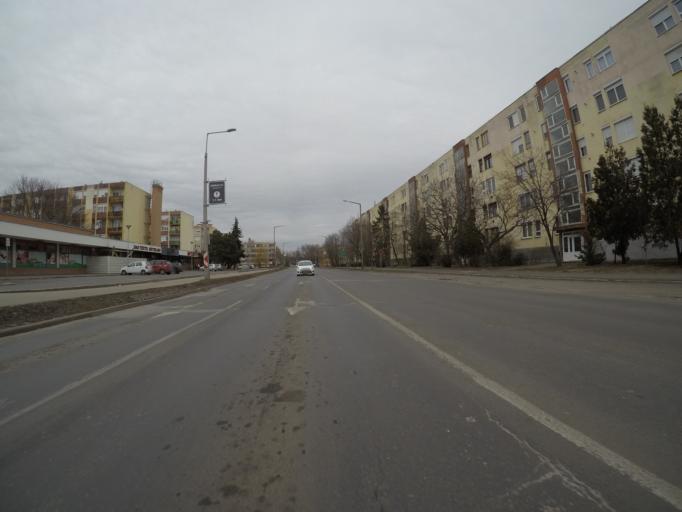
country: HU
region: Jasz-Nagykun-Szolnok
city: Jaszbereny
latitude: 47.4984
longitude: 19.9109
